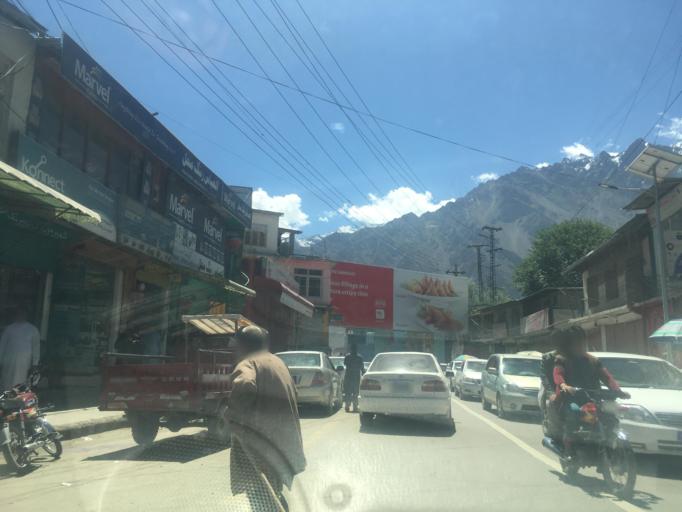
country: PK
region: Gilgit-Baltistan
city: Skardu
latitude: 35.2995
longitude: 75.6344
